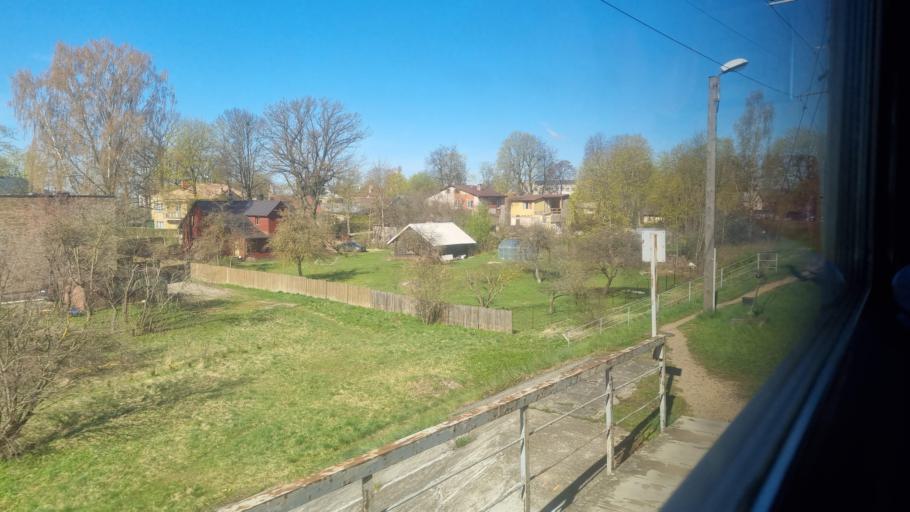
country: LV
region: Ogre
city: Ogre
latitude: 56.8131
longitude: 24.6073
